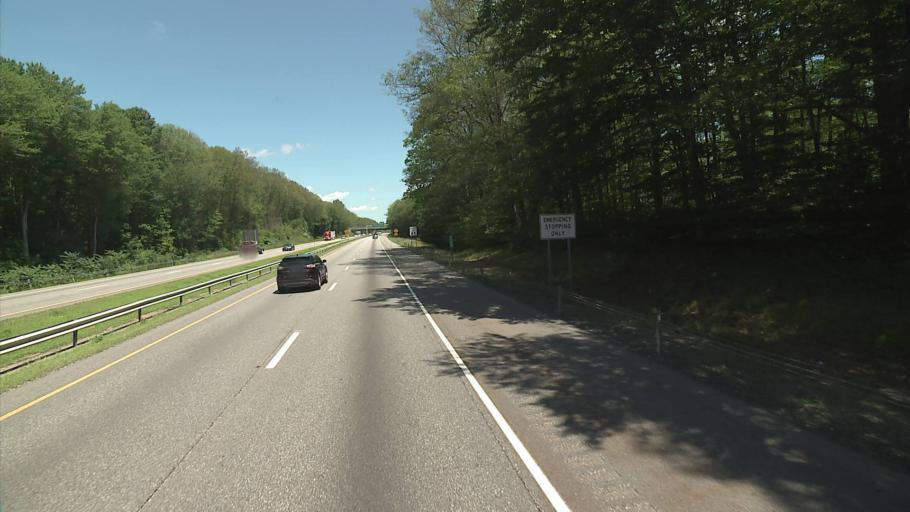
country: US
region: Connecticut
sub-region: New London County
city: Norwich
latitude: 41.5325
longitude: -72.1147
